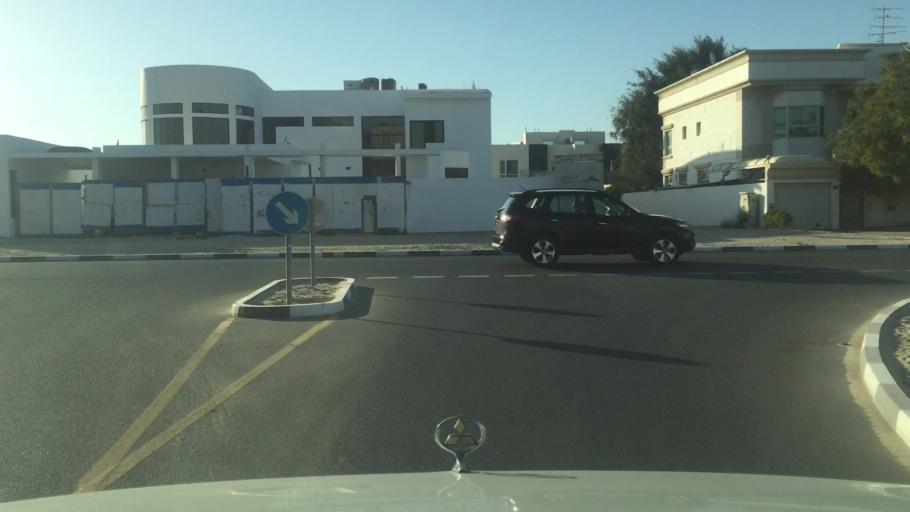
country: AE
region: Dubai
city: Dubai
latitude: 25.1631
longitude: 55.2269
